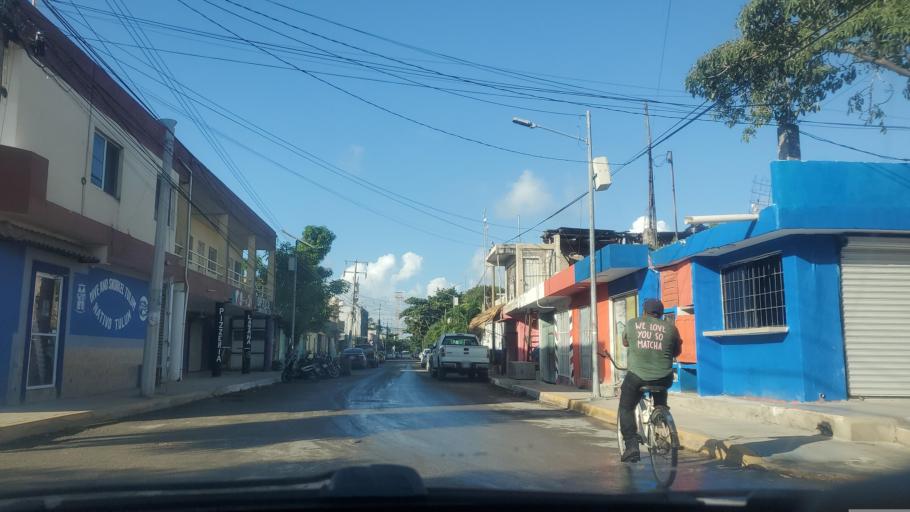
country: MX
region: Quintana Roo
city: Tulum
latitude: 20.2112
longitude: -87.4579
